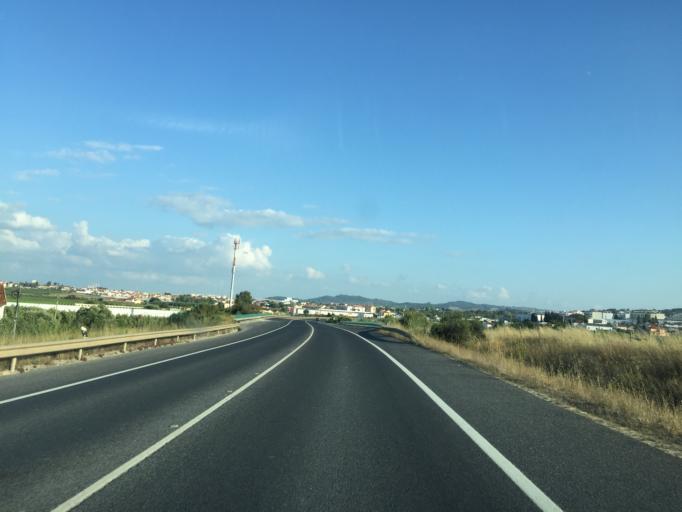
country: PT
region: Lisbon
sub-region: Alenquer
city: Alenquer
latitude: 39.0560
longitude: -8.9953
